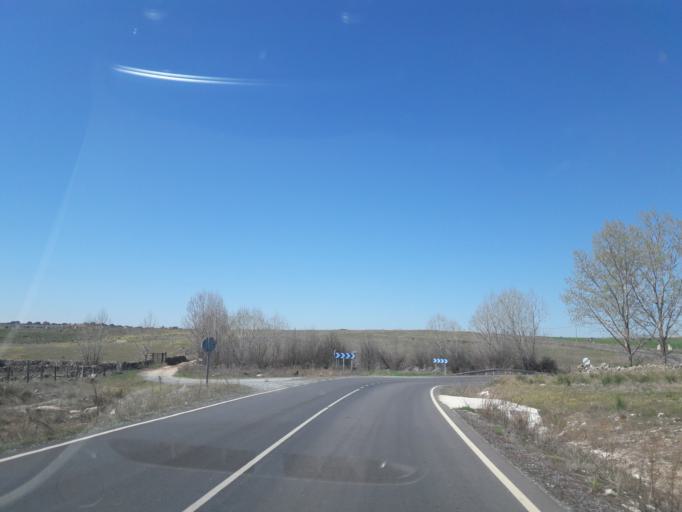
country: ES
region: Castille and Leon
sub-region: Provincia de Salamanca
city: Martinamor
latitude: 40.8071
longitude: -5.6090
